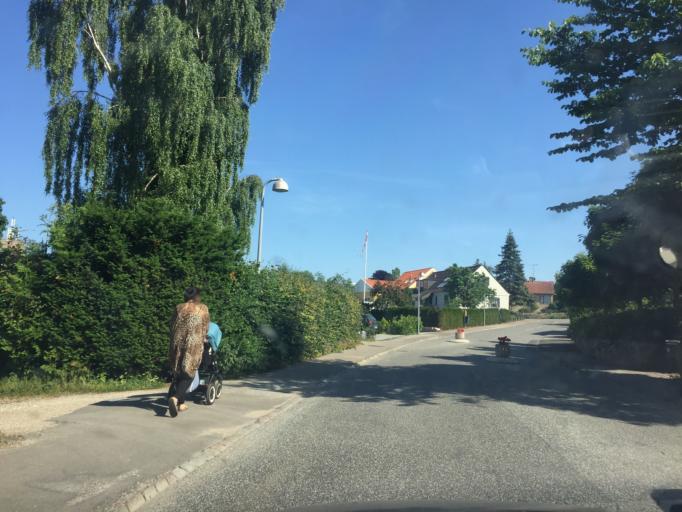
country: DK
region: Capital Region
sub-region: Ballerup Kommune
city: Malov
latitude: 55.7855
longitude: 12.3223
